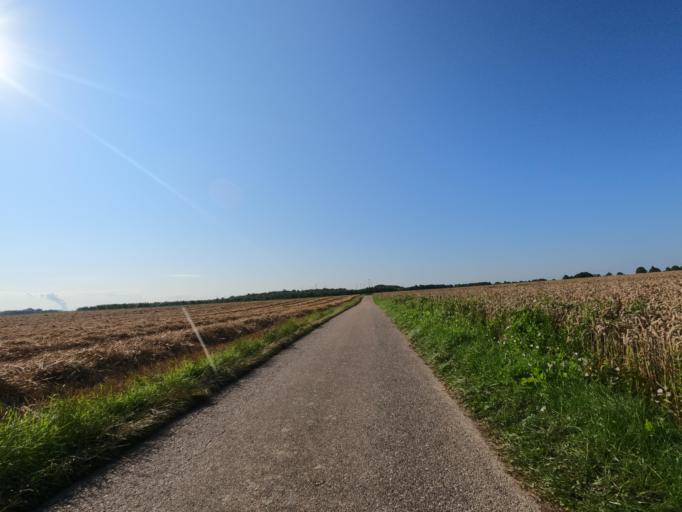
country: DE
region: North Rhine-Westphalia
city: Erkelenz
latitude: 51.0644
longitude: 6.3610
